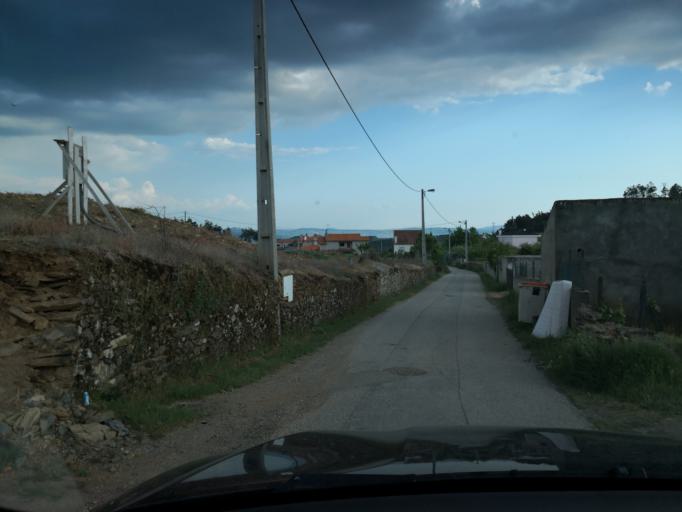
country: PT
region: Vila Real
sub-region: Sabrosa
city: Vilela
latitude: 41.2180
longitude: -7.6685
